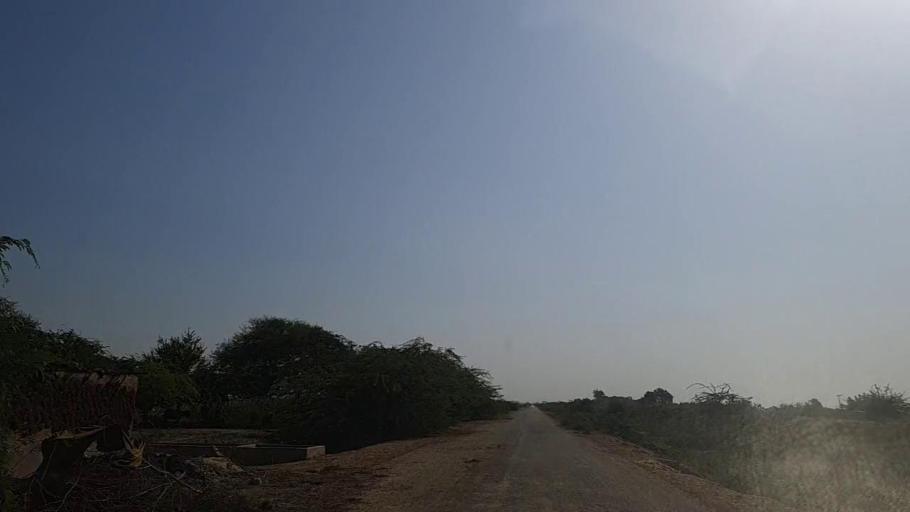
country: PK
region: Sindh
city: Jati
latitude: 24.4545
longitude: 68.2644
